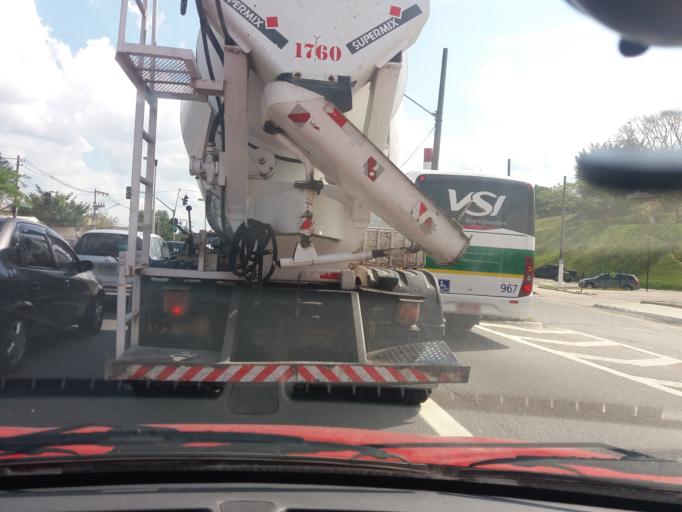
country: BR
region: Sao Paulo
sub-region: Taboao Da Serra
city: Taboao da Serra
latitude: -23.5908
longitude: -46.7370
